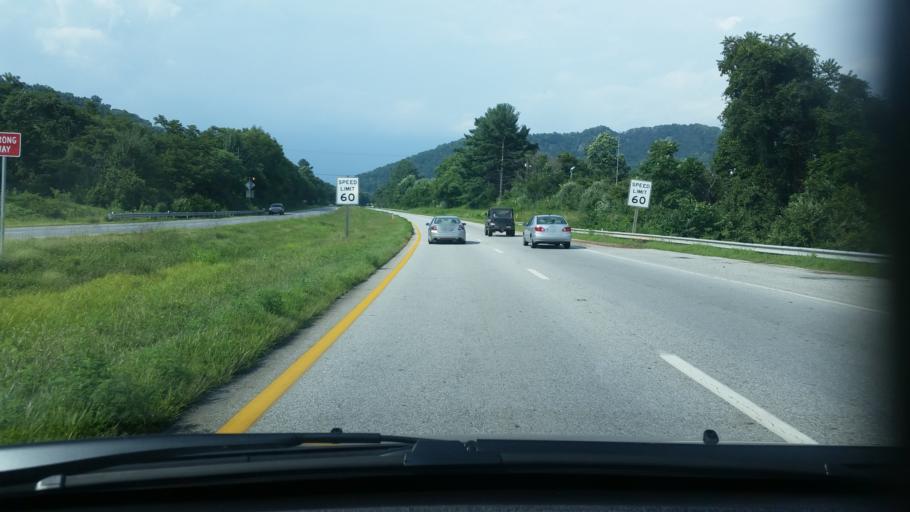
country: US
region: Virginia
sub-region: Nelson County
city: Lovingston
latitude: 37.7533
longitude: -78.8759
